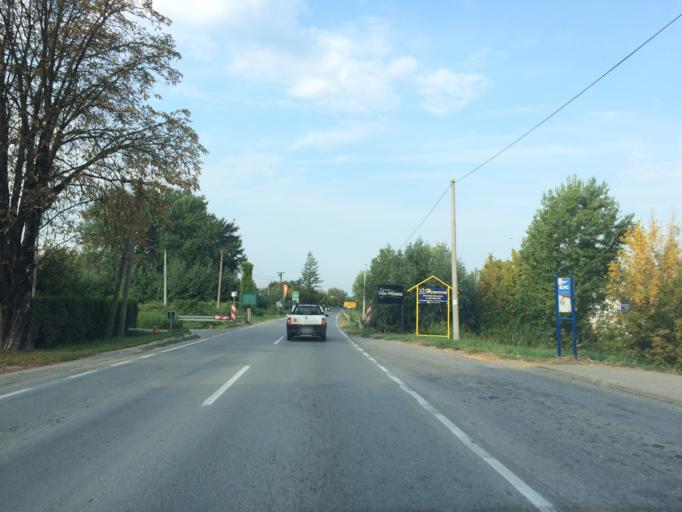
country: RS
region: Autonomna Pokrajina Vojvodina
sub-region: Juznobacki Okrug
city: Novi Sad
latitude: 45.2176
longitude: 19.8150
